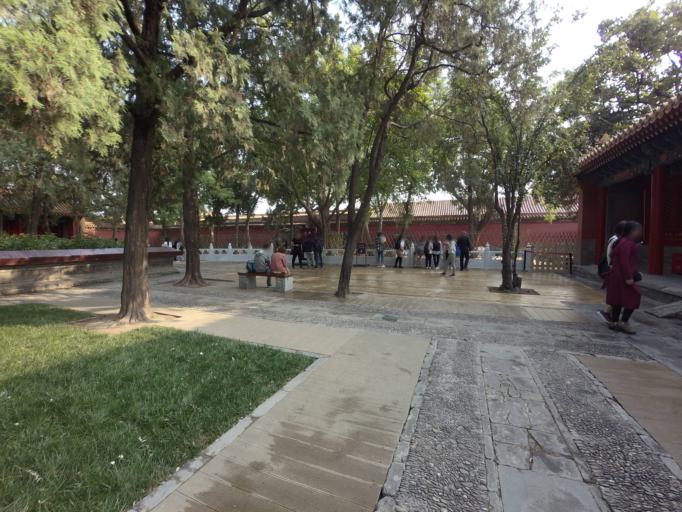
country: CN
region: Beijing
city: Beijing
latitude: 39.9161
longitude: 116.3876
